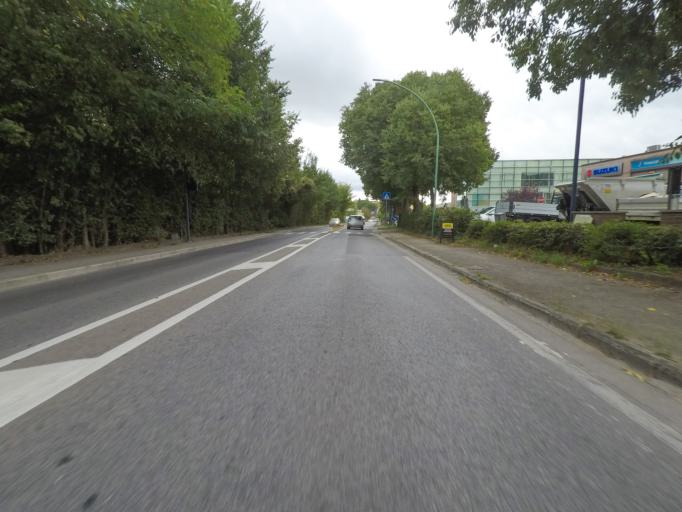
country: IT
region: Tuscany
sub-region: Provincia di Siena
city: Siena
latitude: 43.3230
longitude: 11.3469
